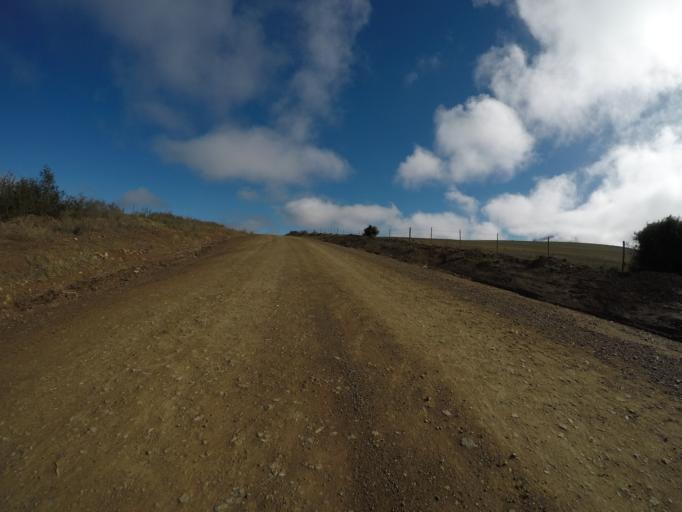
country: ZA
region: Western Cape
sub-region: Overberg District Municipality
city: Caledon
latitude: -34.1094
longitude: 19.7662
